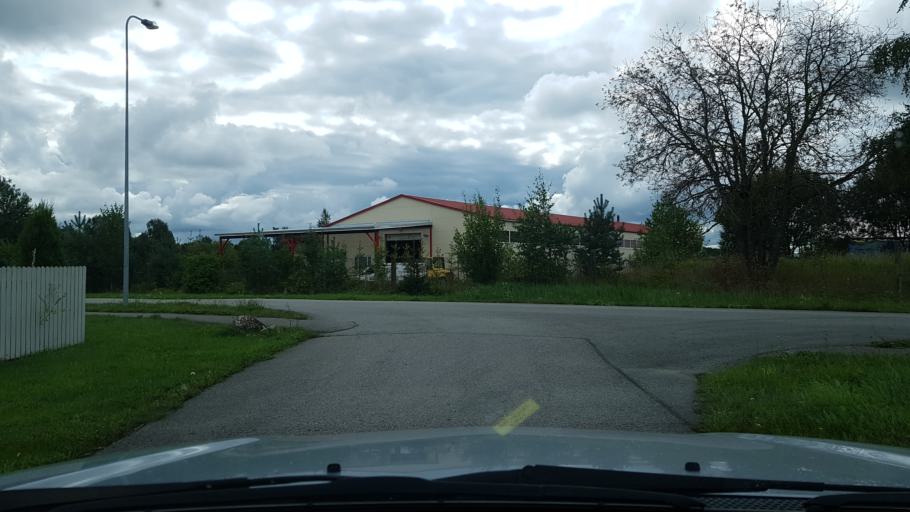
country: EE
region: Harju
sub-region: Rae vald
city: Vaida
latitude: 59.3178
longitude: 24.9434
